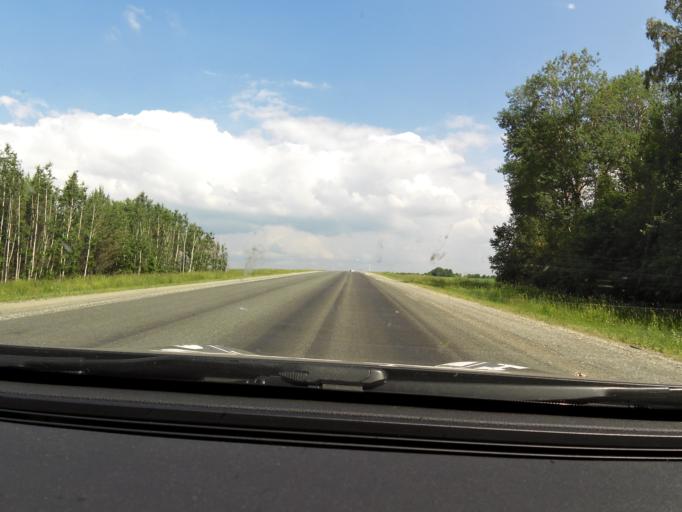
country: RU
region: Sverdlovsk
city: Ufimskiy
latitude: 56.7724
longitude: 58.0387
